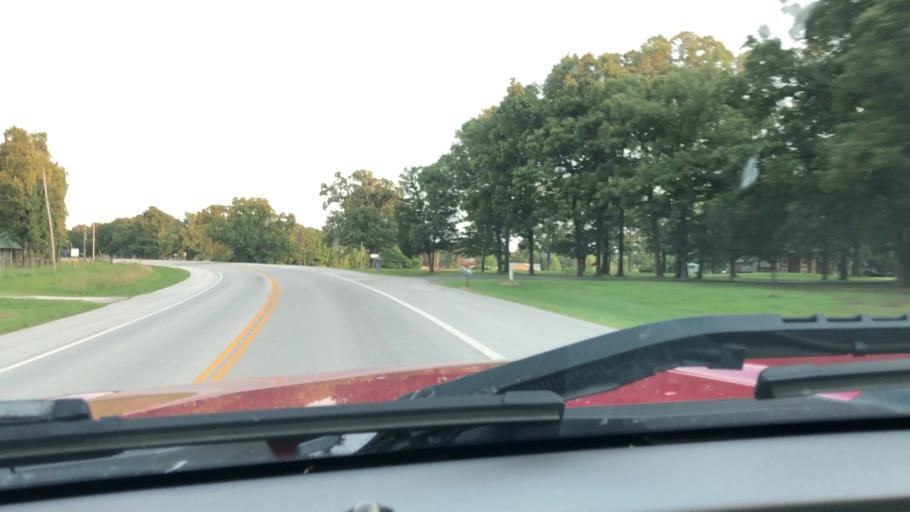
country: US
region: Missouri
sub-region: Jasper County
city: Duquesne
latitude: 36.9784
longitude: -94.4638
